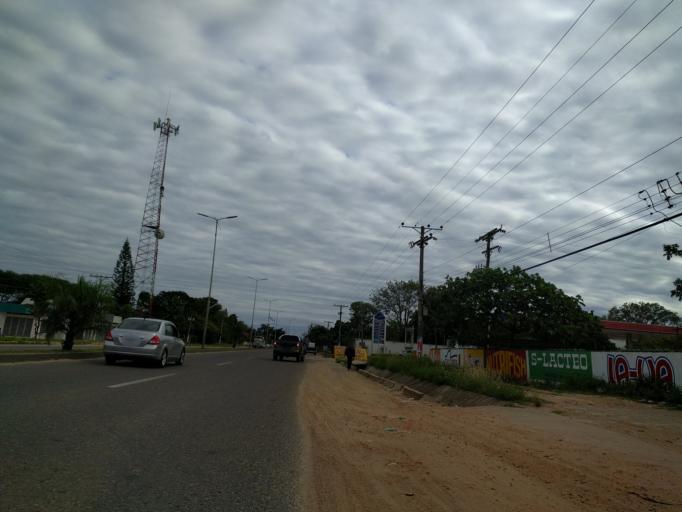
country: BO
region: Santa Cruz
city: Santa Cruz de la Sierra
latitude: -17.8522
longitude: -63.2540
